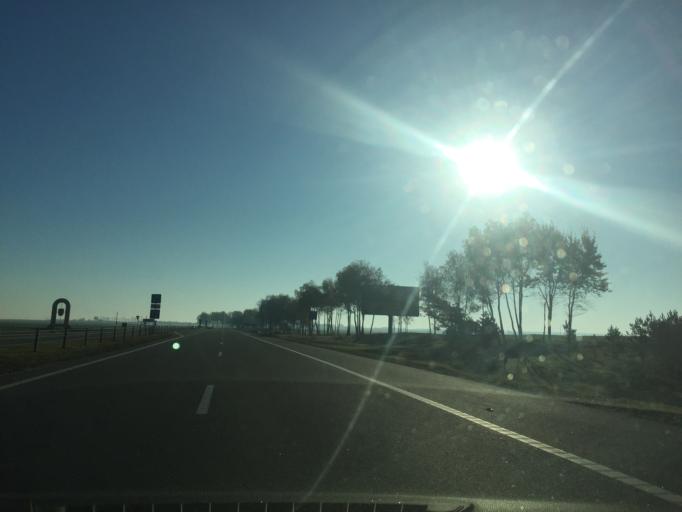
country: BY
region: Minsk
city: Luhavaya Slabada
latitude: 53.7629
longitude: 27.8735
